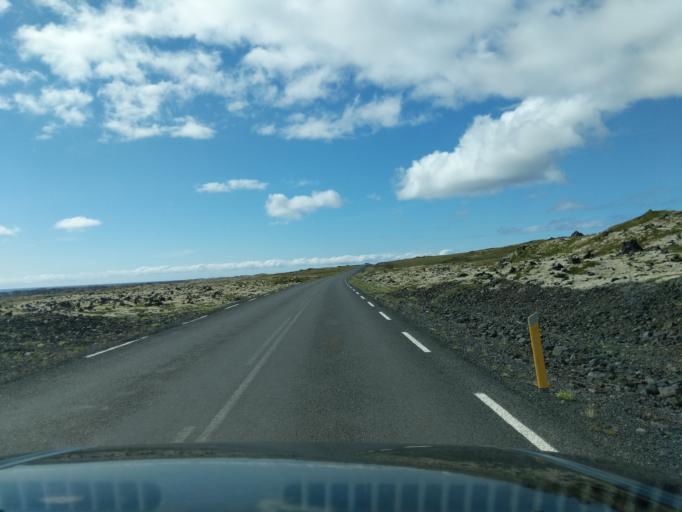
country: IS
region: West
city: Olafsvik
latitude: 64.7577
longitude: -23.8484
